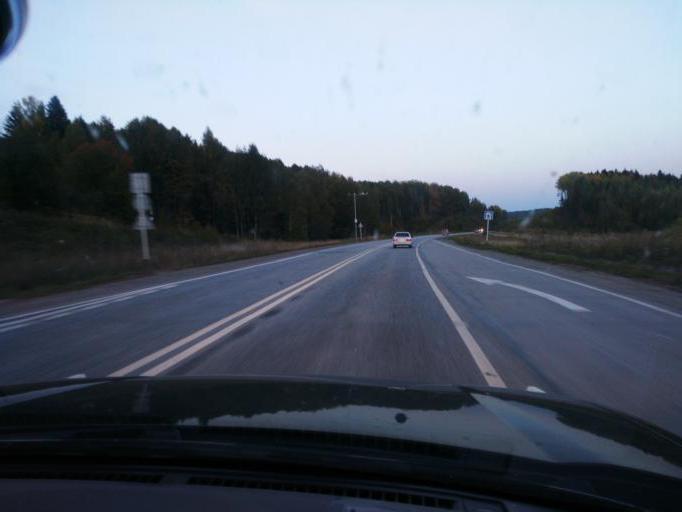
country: RU
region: Perm
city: Verkhnechusovskiye Gorodki
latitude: 58.2962
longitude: 56.8643
